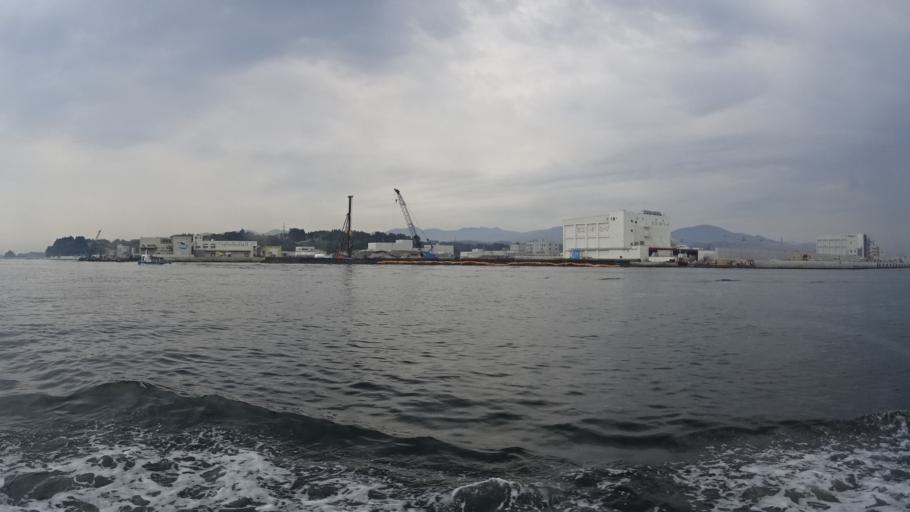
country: JP
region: Iwate
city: Ofunato
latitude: 38.8892
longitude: 141.5961
